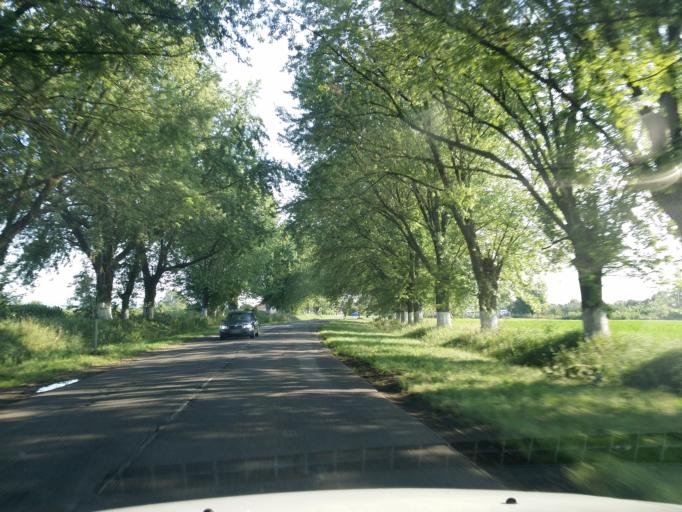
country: HU
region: Borsod-Abauj-Zemplen
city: Gonc
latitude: 48.4265
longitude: 21.2373
